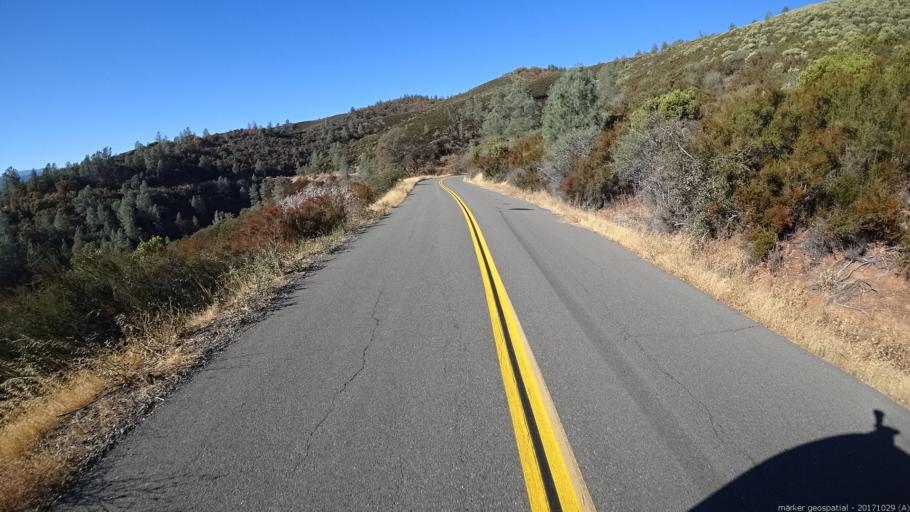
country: US
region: California
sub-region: Trinity County
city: Lewiston
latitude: 40.3815
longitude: -122.8431
